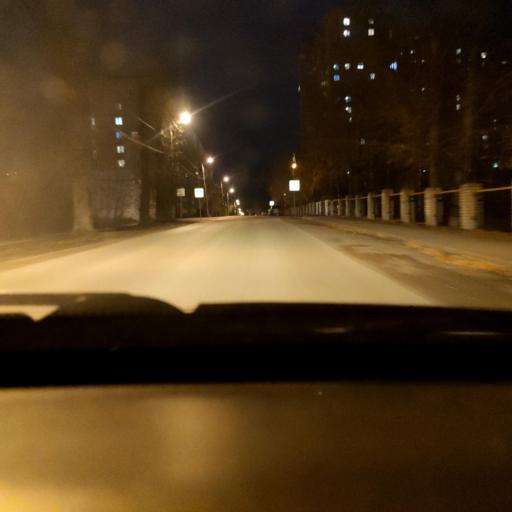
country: RU
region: Perm
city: Perm
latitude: 58.0993
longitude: 56.2997
